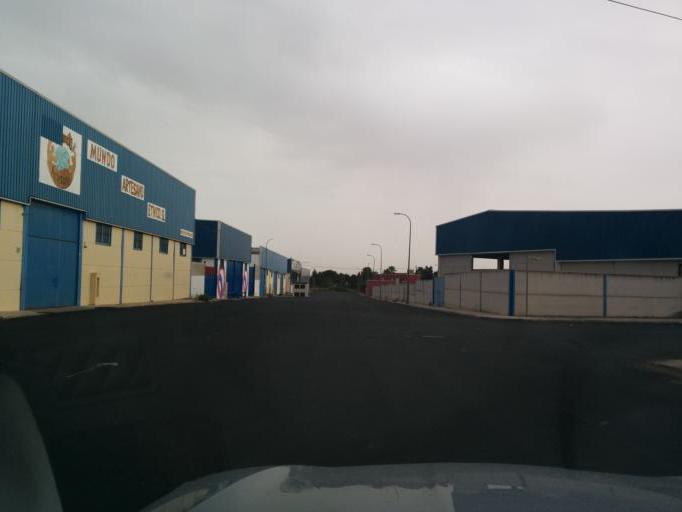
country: ES
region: Andalusia
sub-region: Provincia de Sevilla
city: Guillena
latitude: 37.5579
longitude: -6.0313
